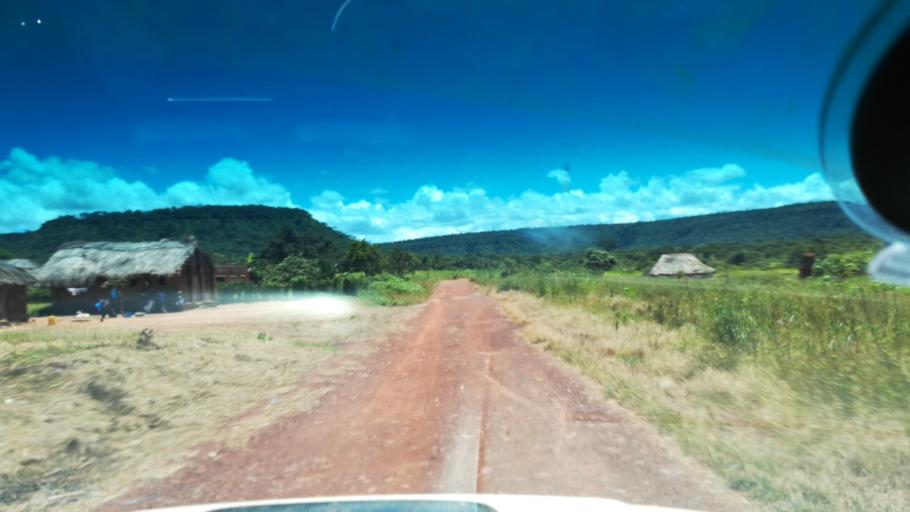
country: ZM
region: Luapula
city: Nchelenge
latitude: -8.8514
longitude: 28.5647
